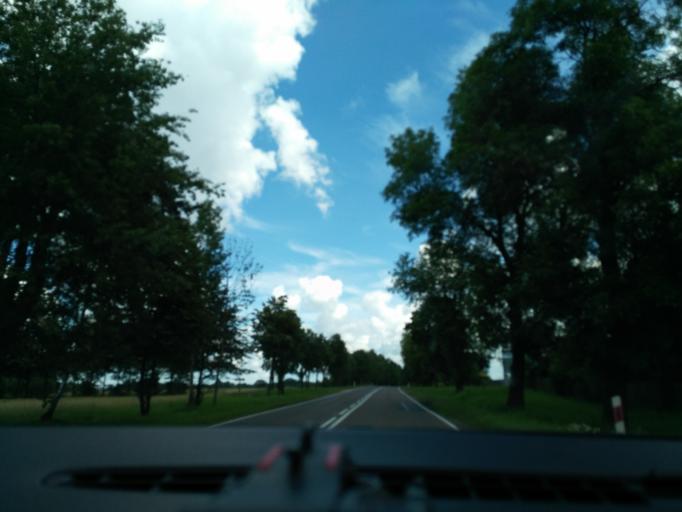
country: PL
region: Podlasie
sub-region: Powiat bielski
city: Bielsk Podlaski
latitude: 52.7263
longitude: 23.1494
